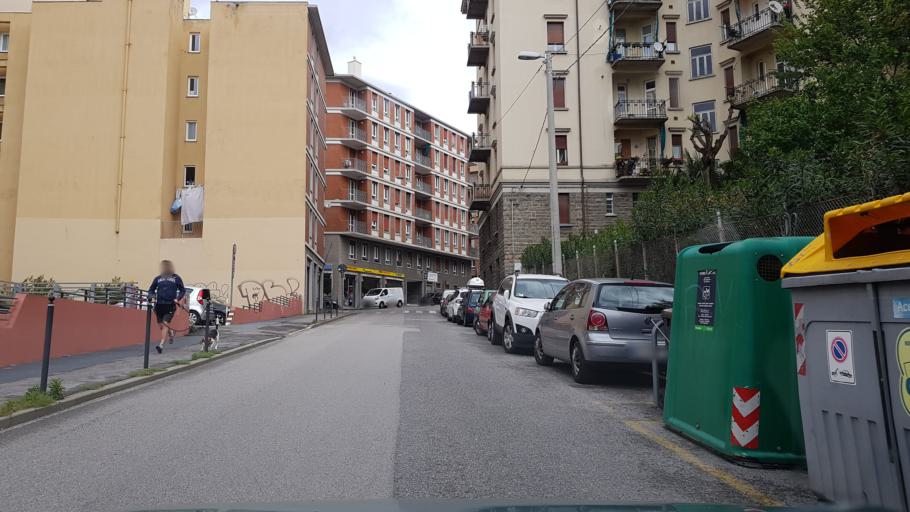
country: IT
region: Friuli Venezia Giulia
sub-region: Provincia di Trieste
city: Trieste
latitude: 45.6562
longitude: 13.7888
